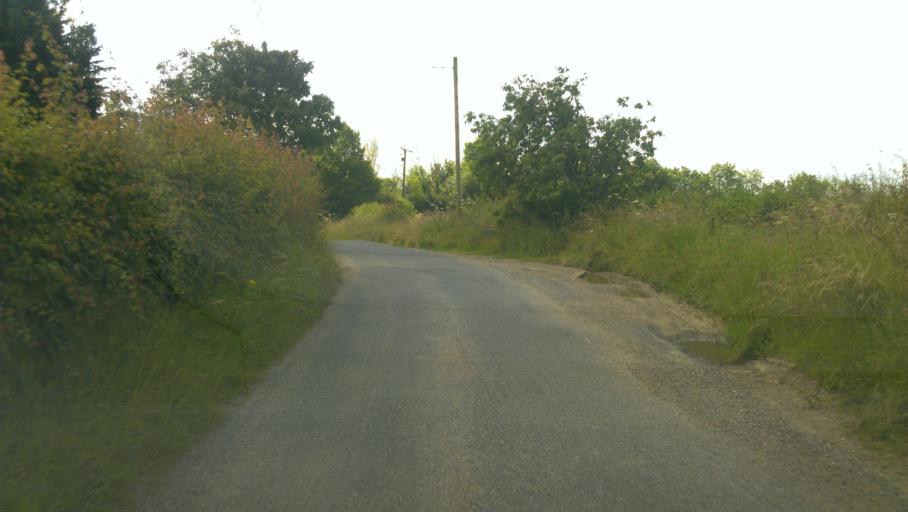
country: GB
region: England
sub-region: Essex
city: Rayne
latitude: 51.8541
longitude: 0.6318
